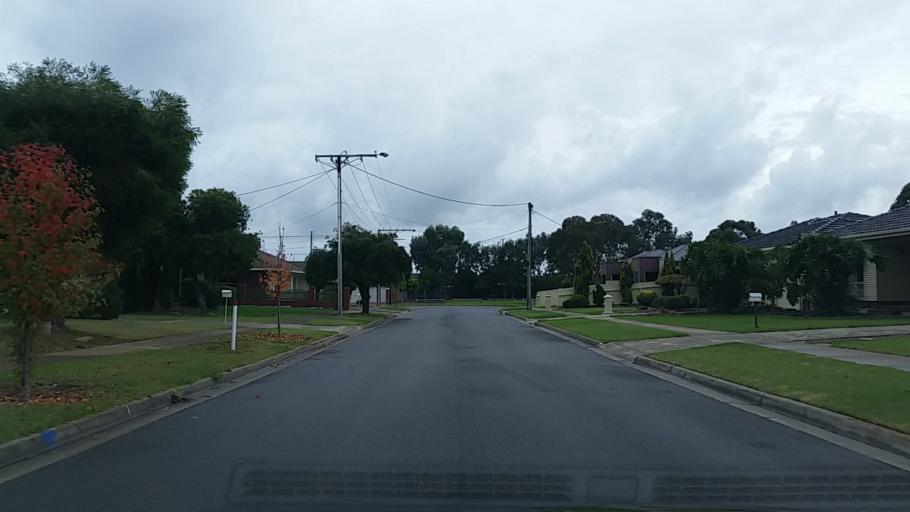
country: AU
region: South Australia
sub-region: Charles Sturt
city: Seaton
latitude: -34.9041
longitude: 138.5080
